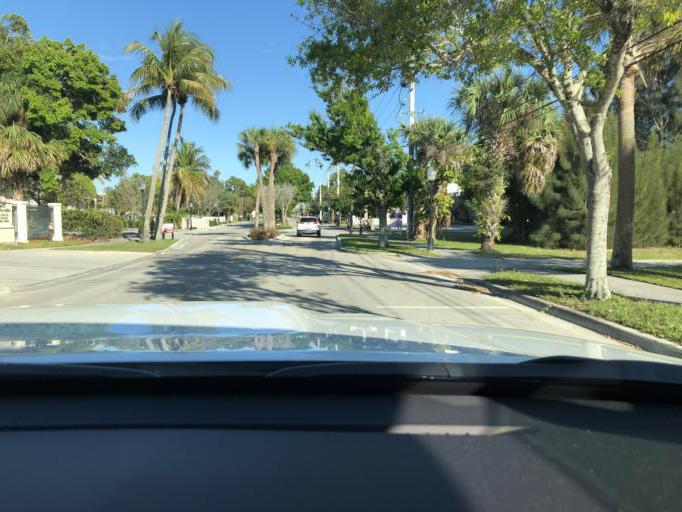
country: US
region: Florida
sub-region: Martin County
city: Stuart
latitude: 27.1984
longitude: -80.2479
